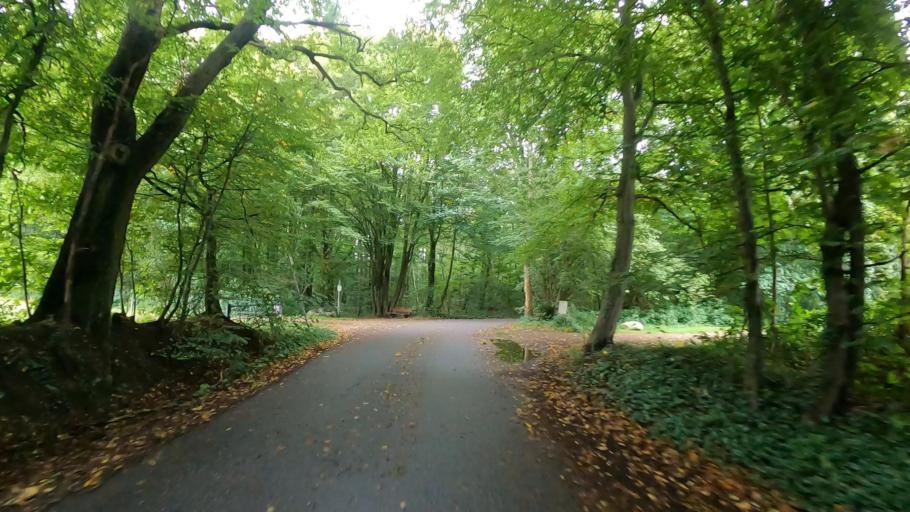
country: DE
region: Schleswig-Holstein
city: Prisdorf
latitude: 53.6710
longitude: 9.7653
